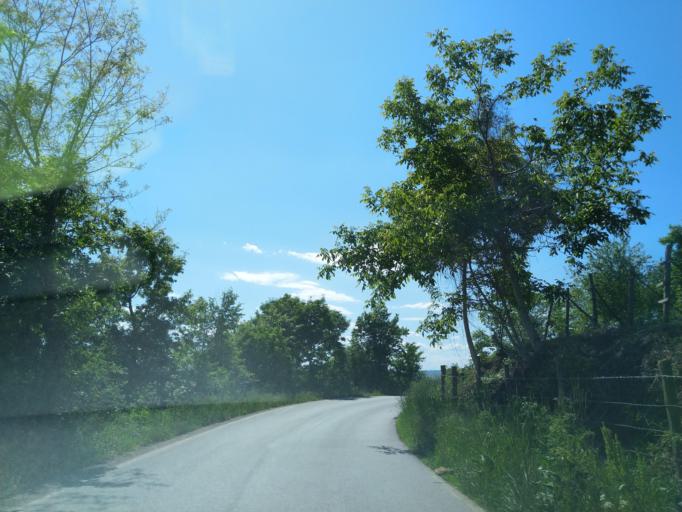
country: RS
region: Central Serbia
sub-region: Zlatiborski Okrug
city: Uzice
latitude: 43.8589
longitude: 19.9088
